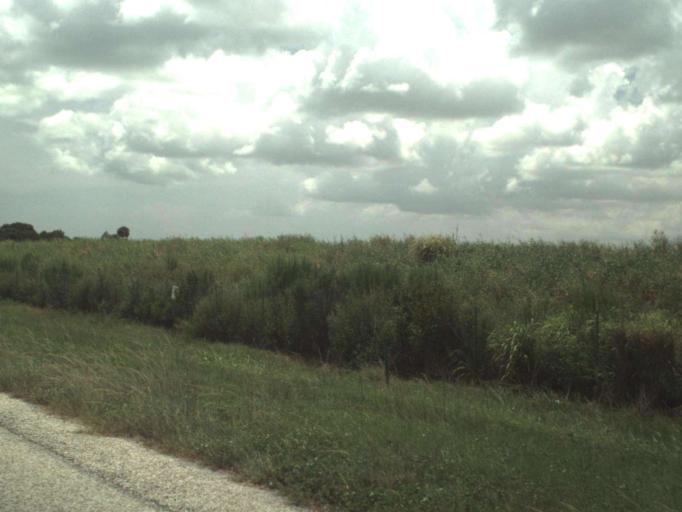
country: US
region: Florida
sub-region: Saint Lucie County
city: Fort Pierce South
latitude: 27.4111
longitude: -80.4111
